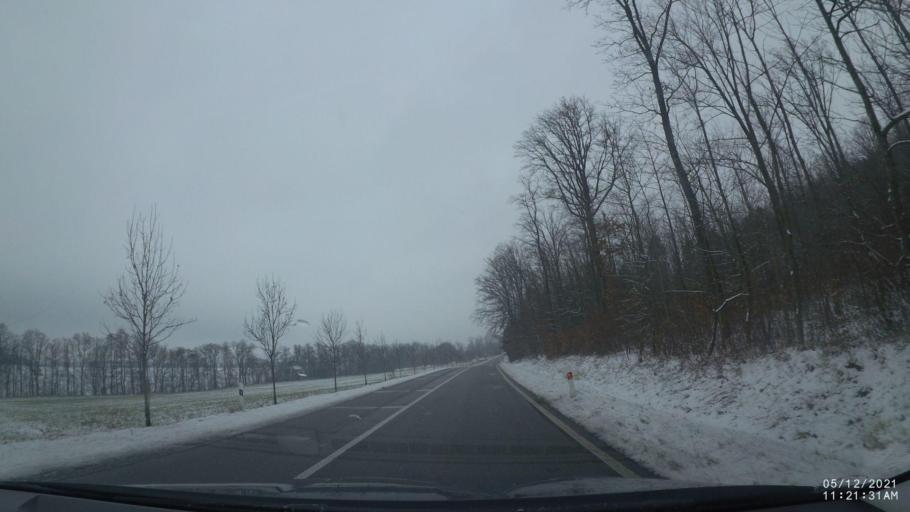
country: CZ
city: Solnice
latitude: 50.1900
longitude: 16.2282
